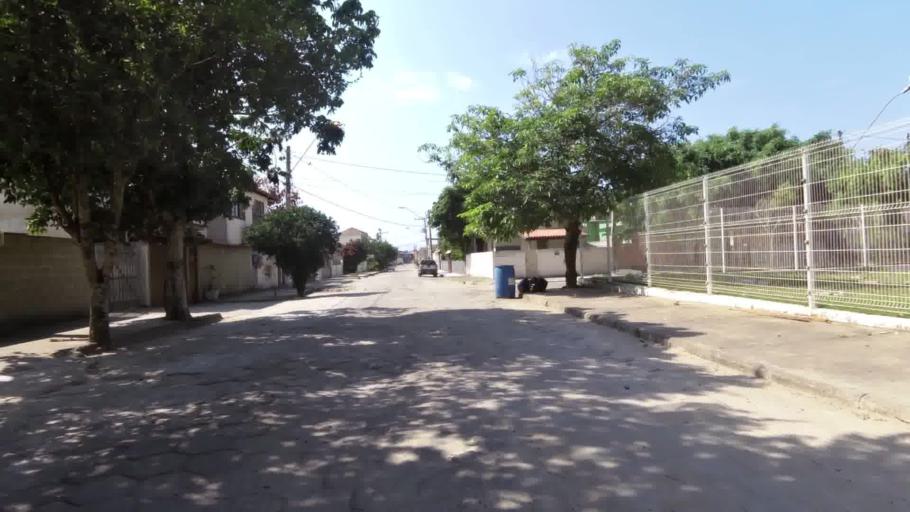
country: BR
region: Espirito Santo
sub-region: Marataizes
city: Marataizes
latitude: -21.0315
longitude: -40.8161
